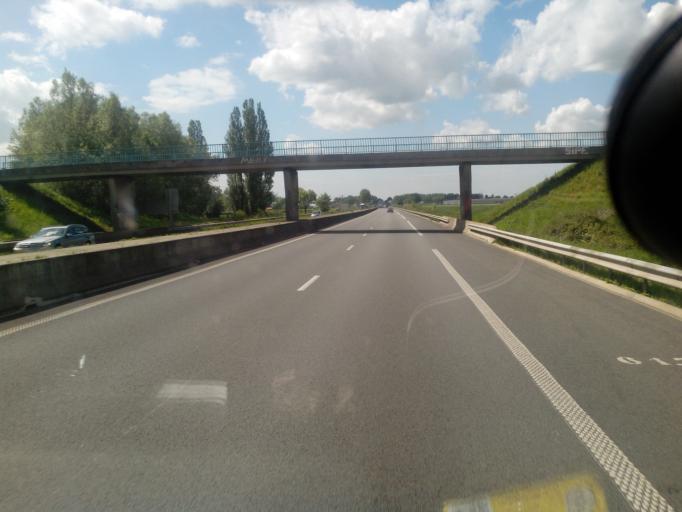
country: FR
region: Nord-Pas-de-Calais
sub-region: Departement du Nord
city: Quaedypre
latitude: 50.9435
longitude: 2.4501
